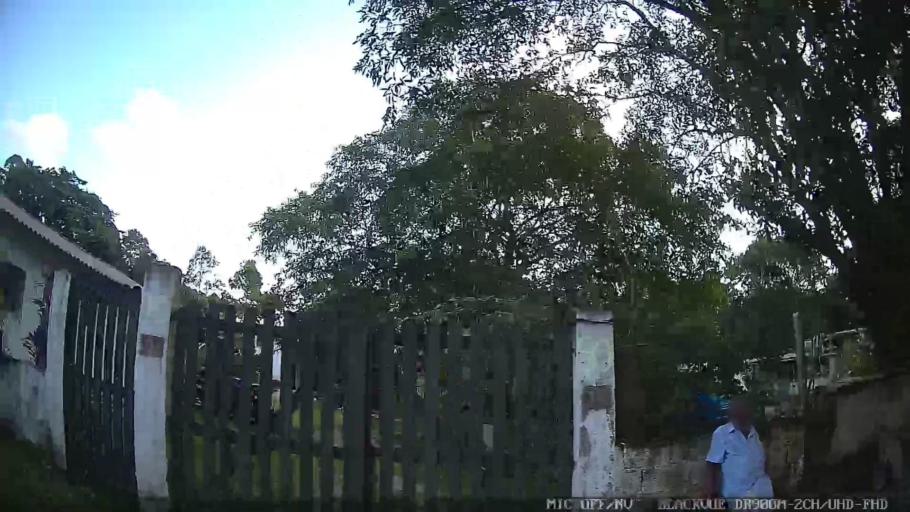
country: BR
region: Sao Paulo
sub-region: Itanhaem
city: Itanhaem
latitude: -24.1627
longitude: -46.8426
